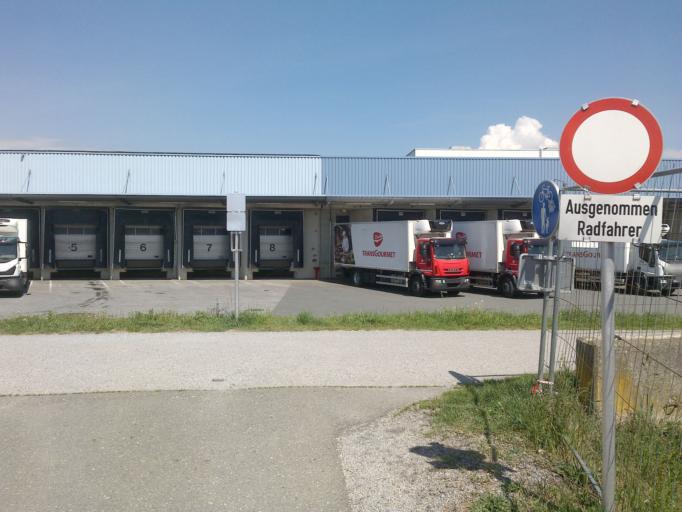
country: AT
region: Styria
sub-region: Politischer Bezirk Graz-Umgebung
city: Seiersberg
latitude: 47.0146
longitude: 15.4122
